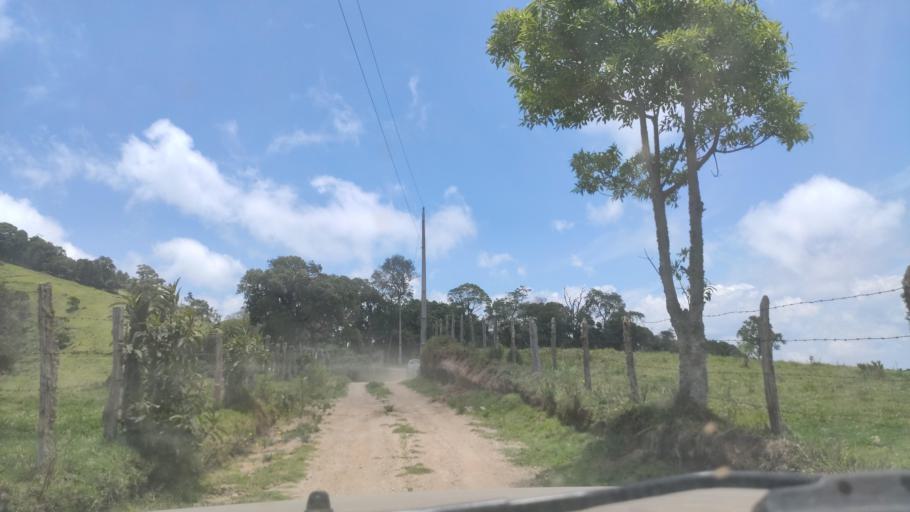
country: BR
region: Minas Gerais
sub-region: Cambui
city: Cambui
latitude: -22.6859
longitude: -45.9564
